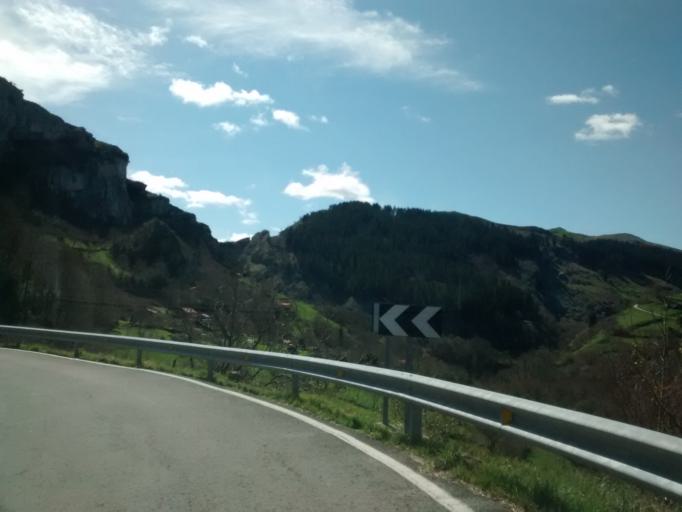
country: ES
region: Cantabria
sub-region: Provincia de Cantabria
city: Lierganes
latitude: 43.2642
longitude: -3.7128
